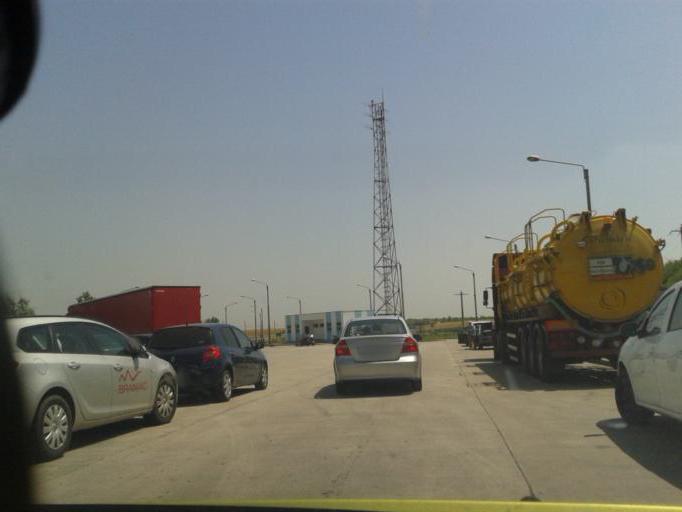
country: RO
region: Calarasi
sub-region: Comuna Sarulesti
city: Sarulesti-Gara
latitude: 44.4422
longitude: 26.6802
